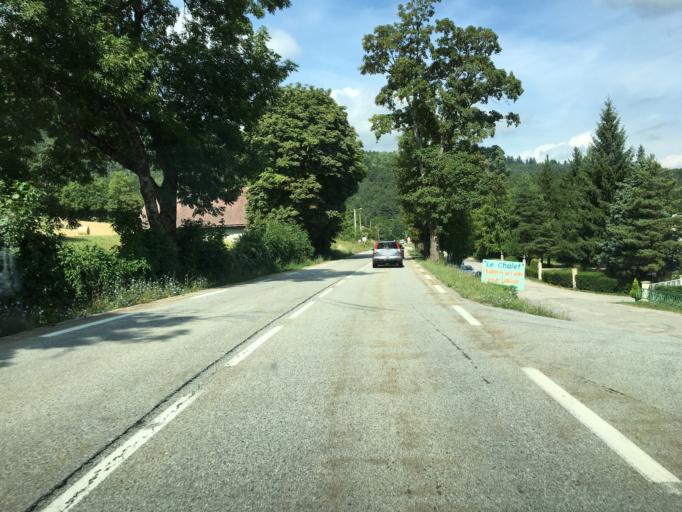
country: FR
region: Rhone-Alpes
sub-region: Departement de l'Isere
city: Mens
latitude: 44.7610
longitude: 5.6631
